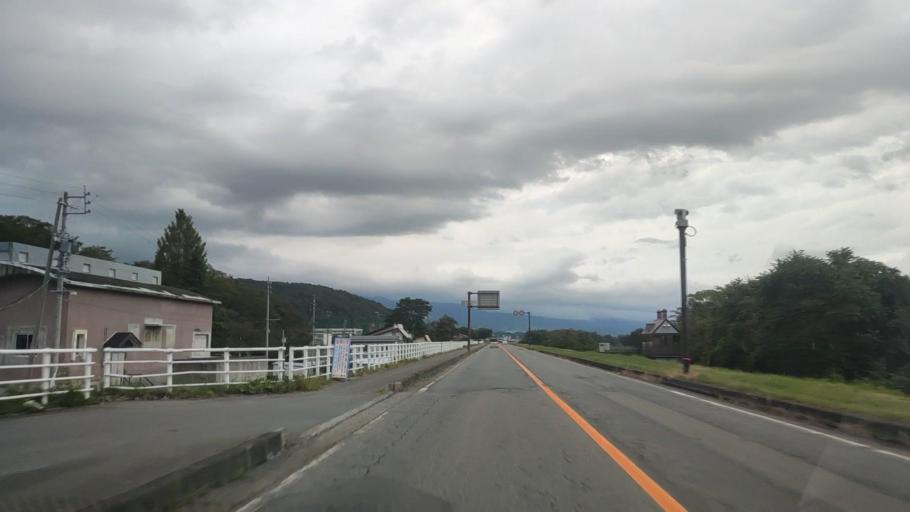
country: JP
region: Nagano
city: Iiyama
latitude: 36.8551
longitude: 138.3678
